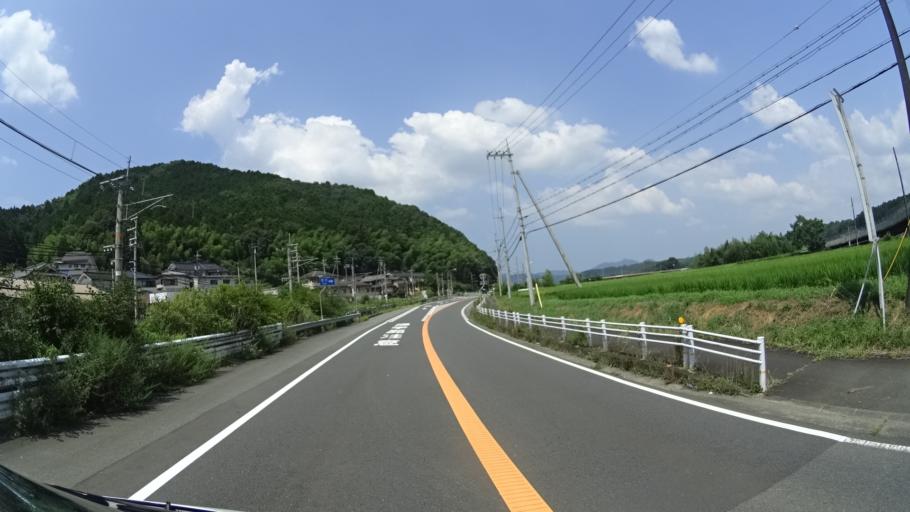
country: JP
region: Kyoto
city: Fukuchiyama
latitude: 35.2782
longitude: 135.1368
